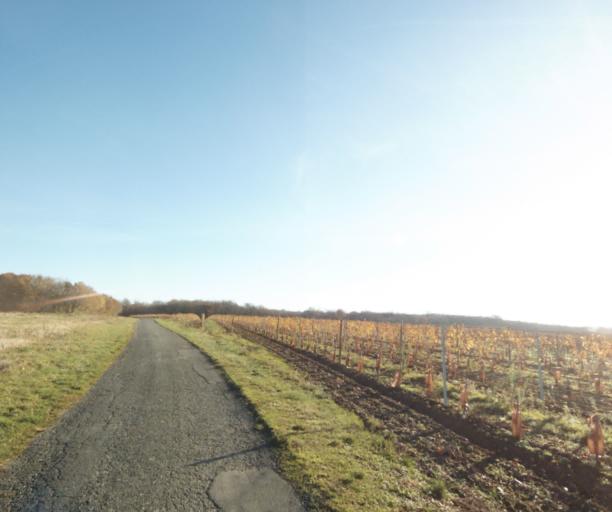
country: FR
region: Poitou-Charentes
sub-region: Departement de la Charente-Maritime
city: Cherac
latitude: 45.7308
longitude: -0.4694
